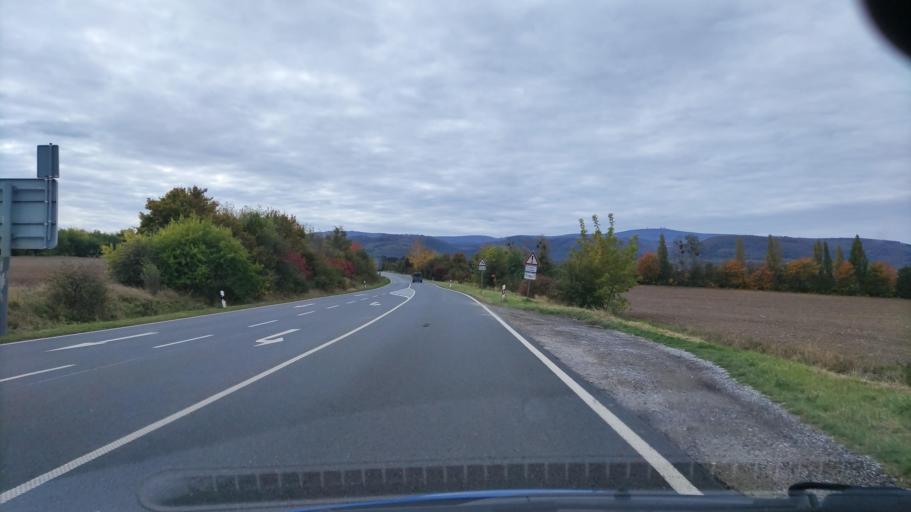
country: DE
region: Saxony-Anhalt
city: Darlingerode
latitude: 51.8695
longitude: 10.7591
